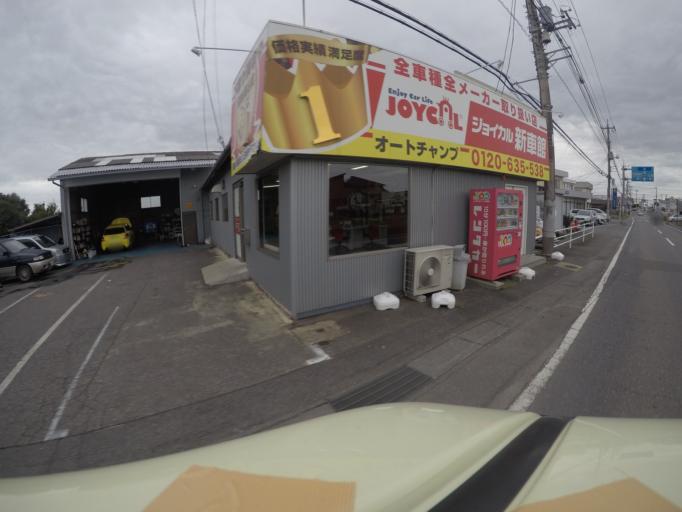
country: JP
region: Ibaraki
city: Naka
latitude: 36.0860
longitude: 140.1295
